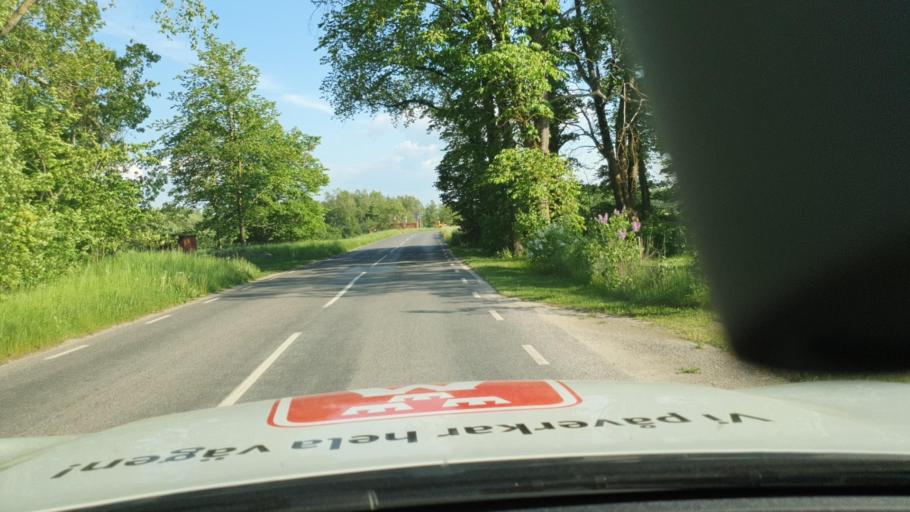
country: SE
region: Vaestra Goetaland
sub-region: Falkopings Kommun
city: Akarp
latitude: 58.1824
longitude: 13.6322
